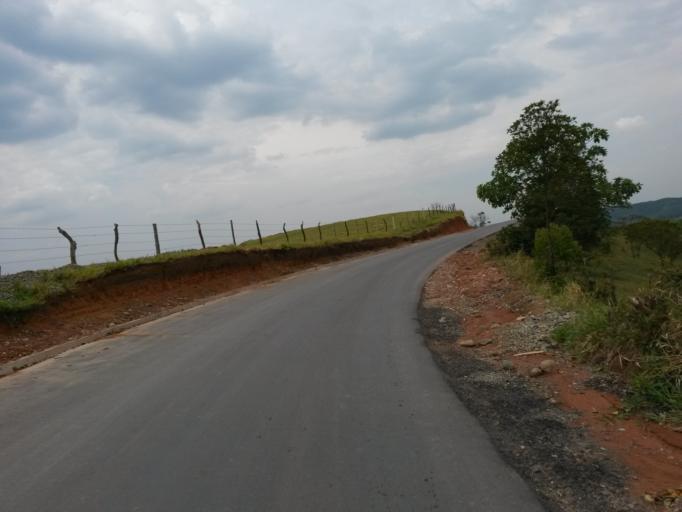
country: CO
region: Cauca
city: Buenos Aires
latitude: 3.0854
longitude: -76.6085
